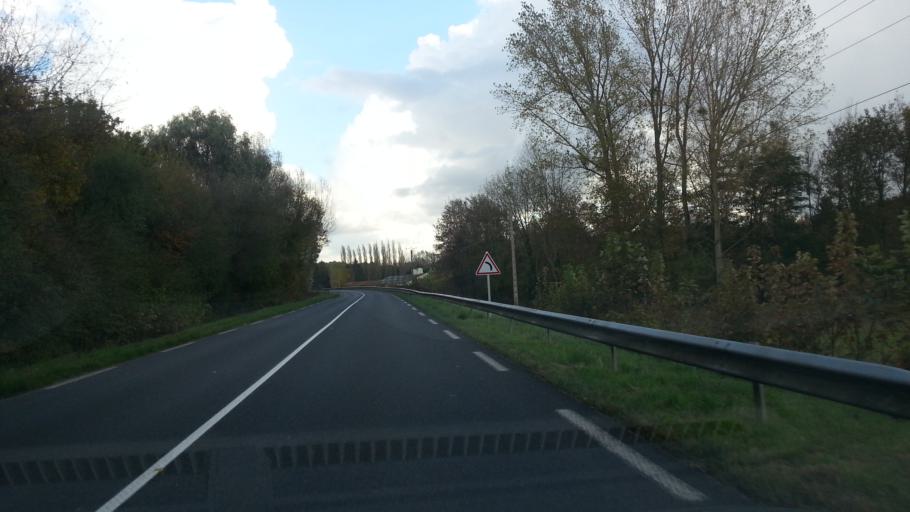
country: FR
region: Picardie
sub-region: Departement de l'Oise
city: Balagny-sur-Therain
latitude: 49.2950
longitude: 2.3491
